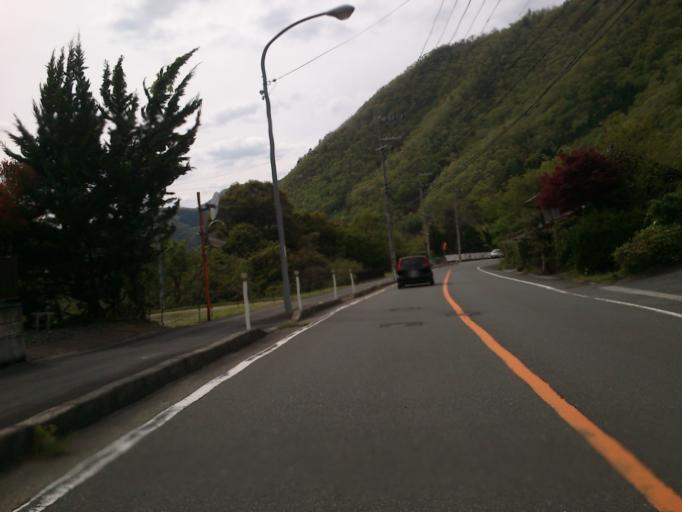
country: JP
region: Kyoto
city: Ayabe
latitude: 35.2682
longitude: 135.4746
